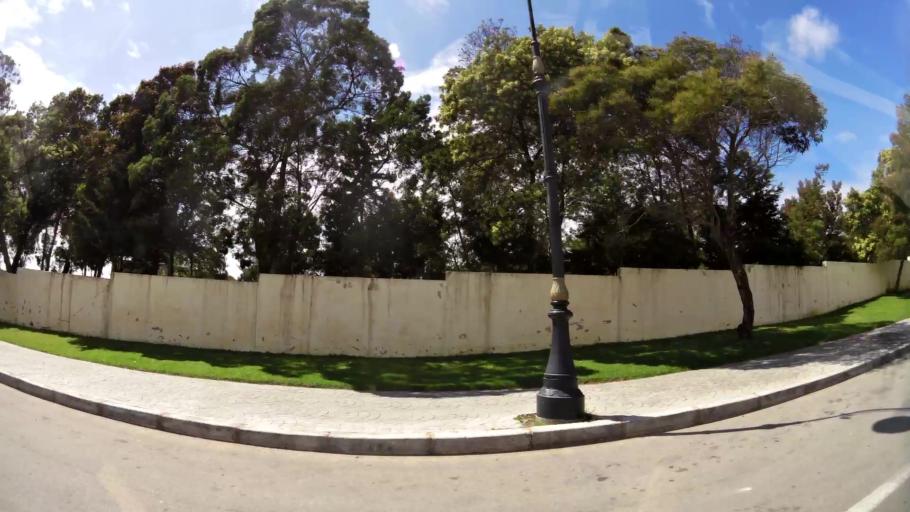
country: MA
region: Tanger-Tetouan
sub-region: Tanger-Assilah
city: Boukhalef
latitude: 35.7866
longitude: -5.8669
